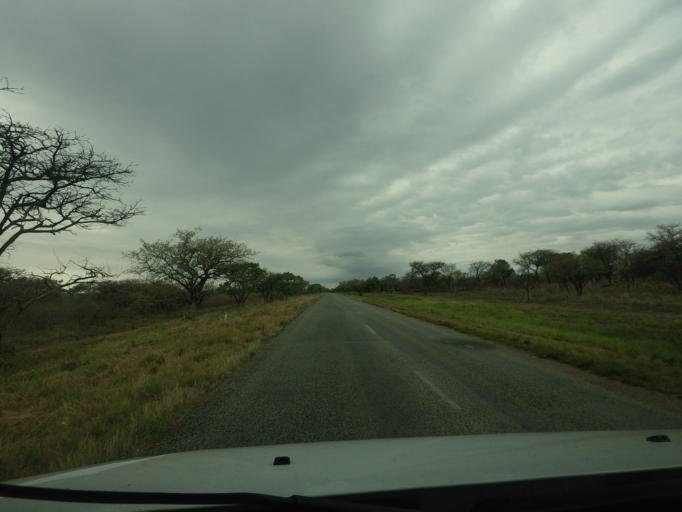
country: ZA
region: Limpopo
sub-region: Mopani District Municipality
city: Hoedspruit
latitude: -24.5077
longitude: 30.9327
